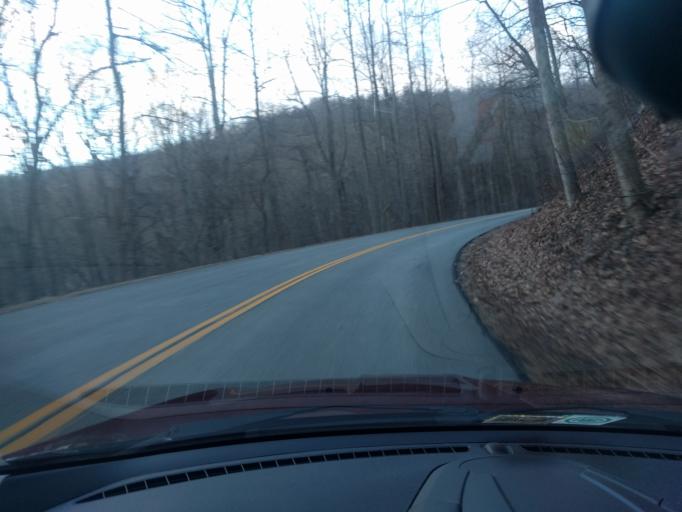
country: US
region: Virginia
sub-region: Botetourt County
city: Buchanan
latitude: 37.4644
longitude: -79.6340
